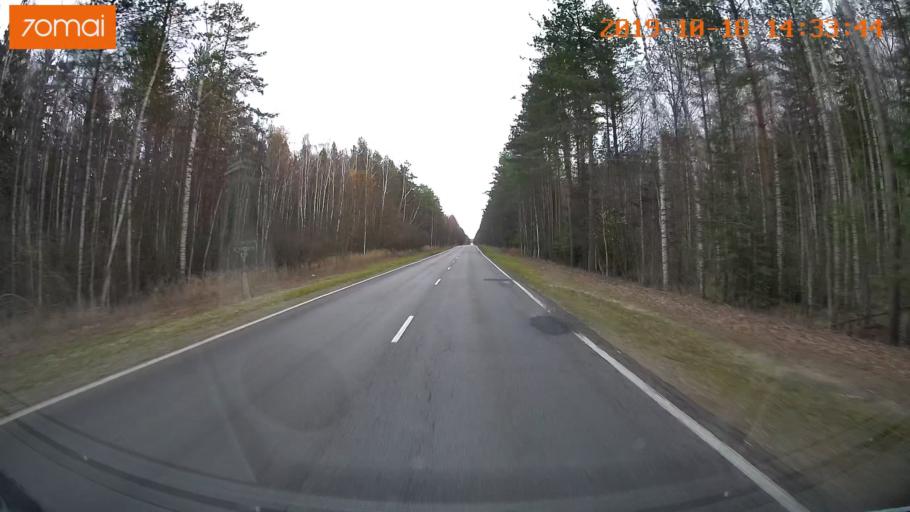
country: RU
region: Rjazan
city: Tuma
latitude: 55.2046
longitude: 40.6024
